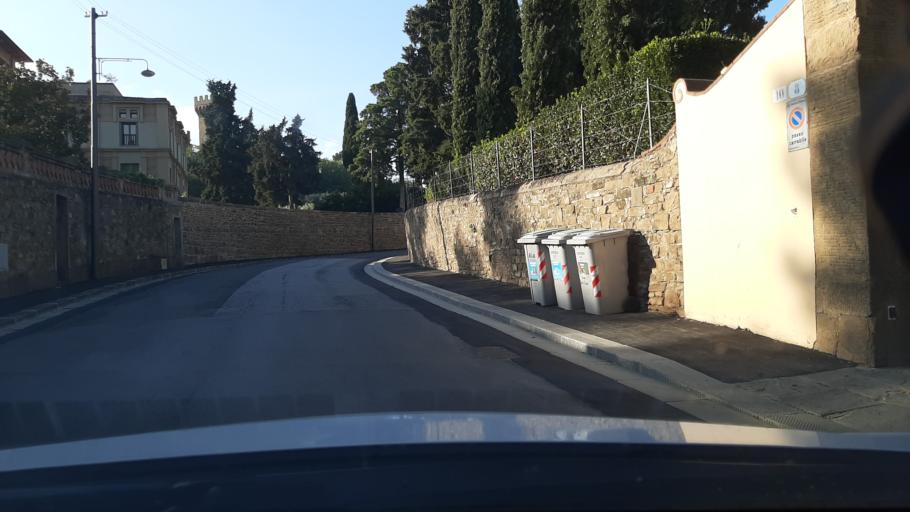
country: IT
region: Tuscany
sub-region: Province of Florence
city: Florence
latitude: 43.7545
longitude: 11.2591
